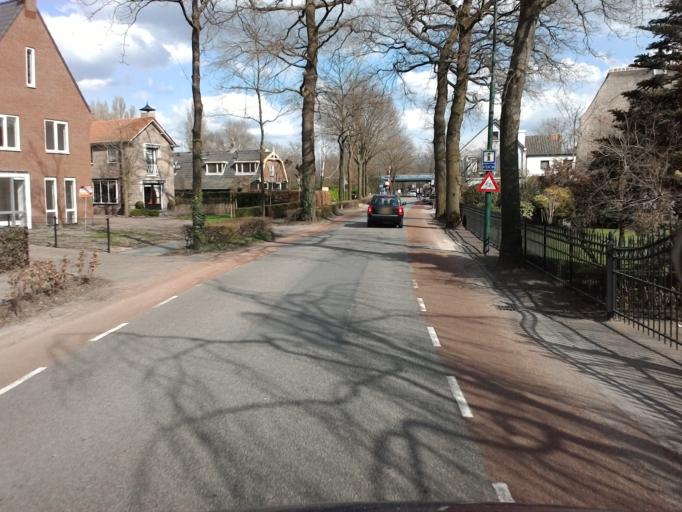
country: NL
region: North Holland
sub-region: Gemeente Wijdemeren
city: Nieuw-Loosdrecht
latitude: 52.1585
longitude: 5.1656
